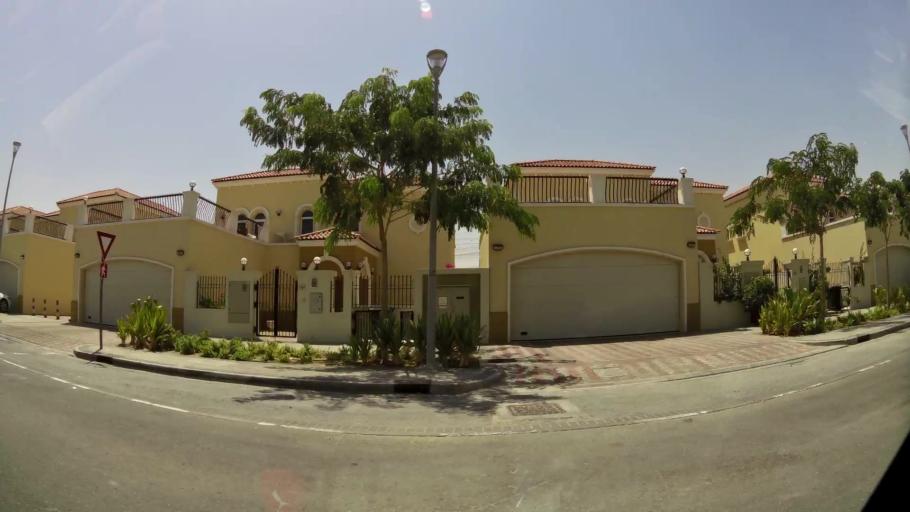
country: AE
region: Dubai
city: Dubai
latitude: 25.0369
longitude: 55.1687
